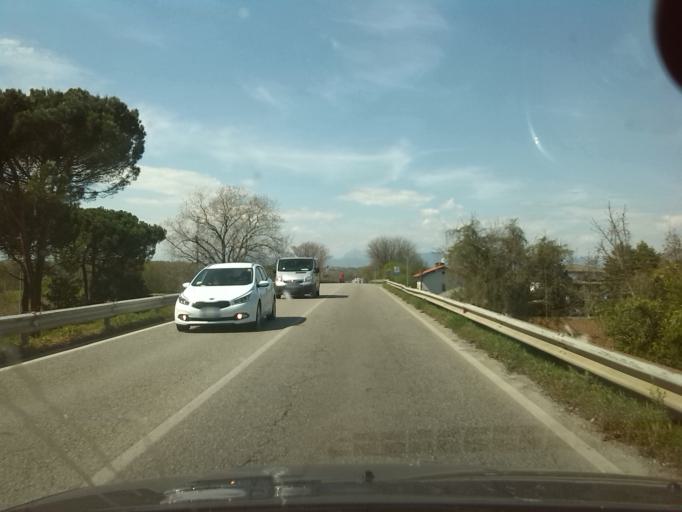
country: IT
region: Friuli Venezia Giulia
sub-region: Provincia di Udine
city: Colugna
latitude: 46.0983
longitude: 13.2090
